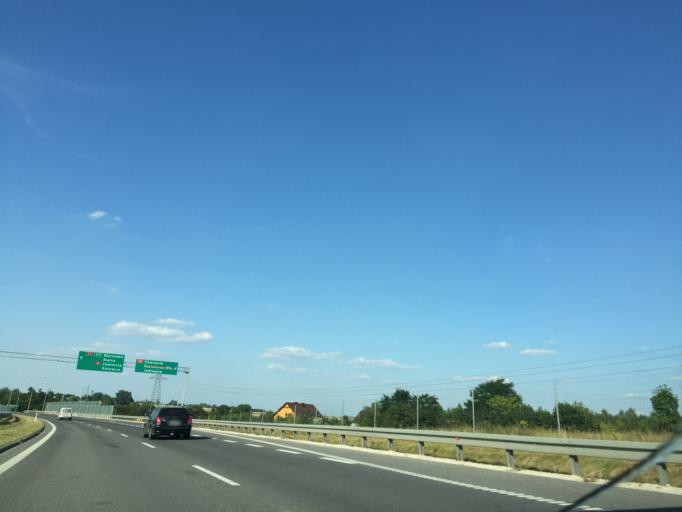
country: PL
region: Swietokrzyskie
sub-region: Powiat jedrzejowski
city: Jedrzejow
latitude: 50.6299
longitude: 20.3149
